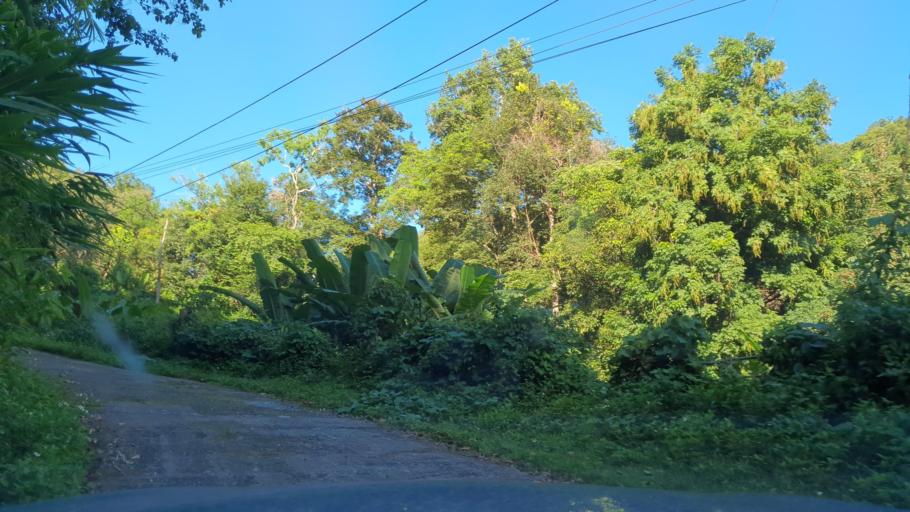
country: TH
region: Chiang Mai
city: Mae On
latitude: 18.8135
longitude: 99.3330
